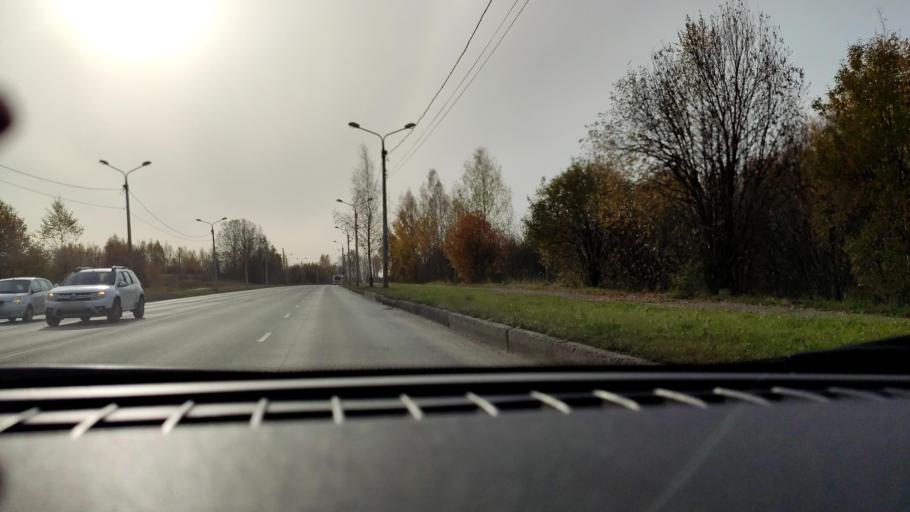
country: RU
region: Perm
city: Perm
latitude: 58.0690
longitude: 56.3666
